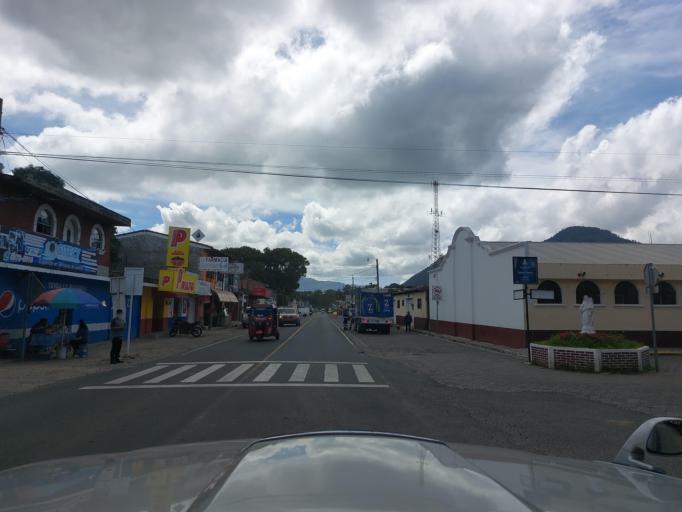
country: GT
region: Chimaltenango
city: Parramos
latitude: 14.6099
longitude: -90.8019
